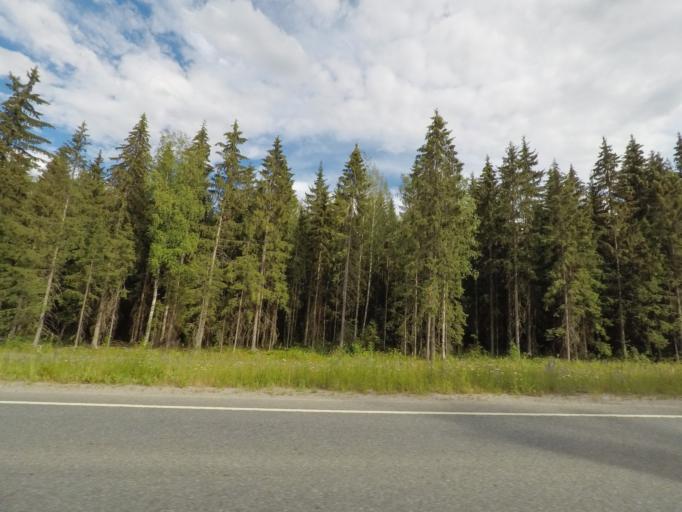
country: FI
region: Paijanne Tavastia
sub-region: Lahti
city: Lahti
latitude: 60.9432
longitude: 25.6021
